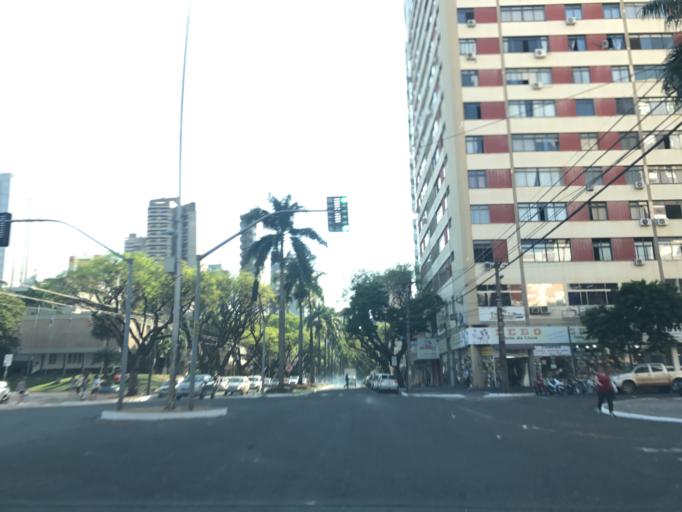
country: BR
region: Parana
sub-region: Maringa
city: Maringa
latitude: -23.4237
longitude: -51.9379
